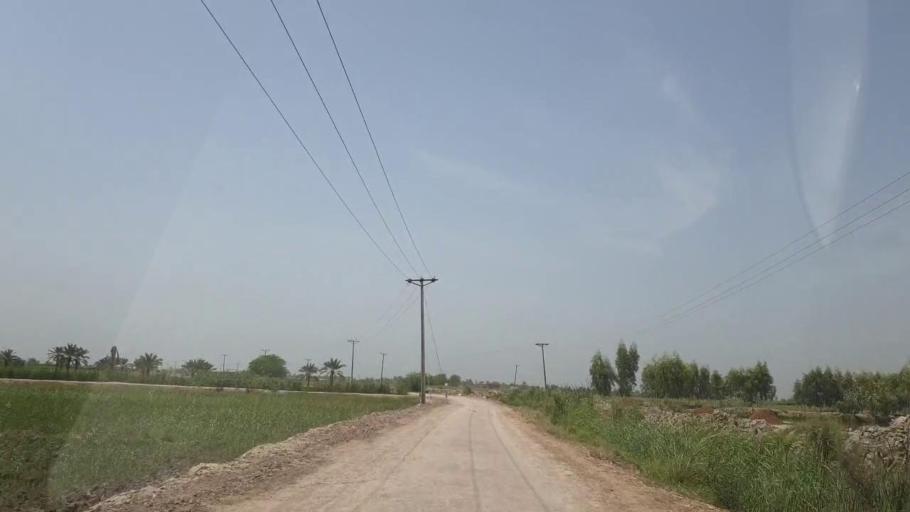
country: PK
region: Sindh
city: Ranipur
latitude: 27.3058
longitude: 68.5456
